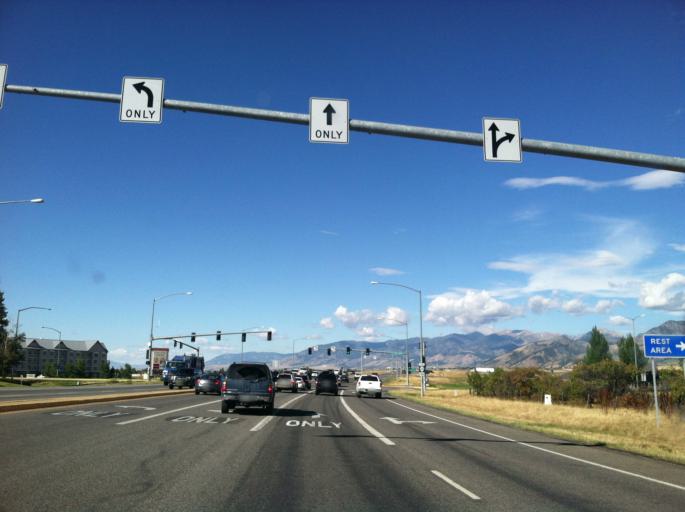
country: US
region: Montana
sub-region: Gallatin County
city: Bozeman
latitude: 45.7110
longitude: -111.0654
